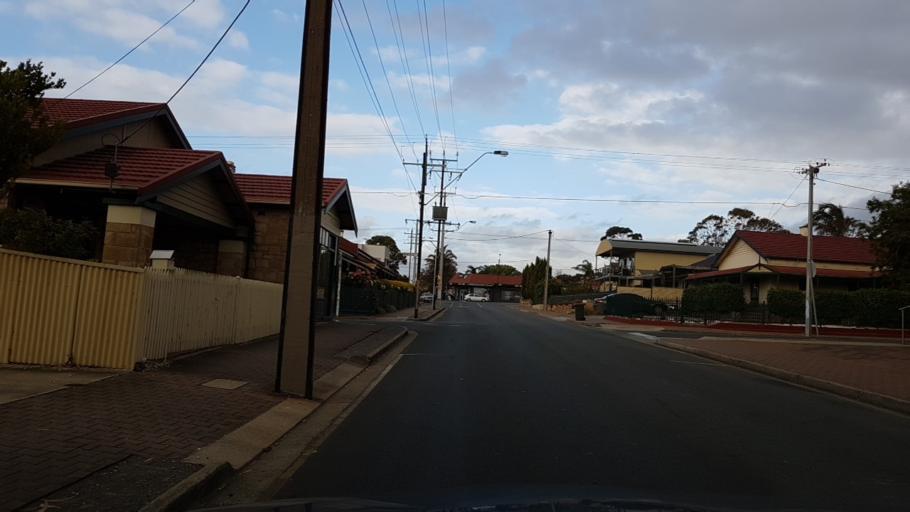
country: AU
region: South Australia
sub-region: Adelaide Hills
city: Seacliff
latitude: -35.0315
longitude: 138.5228
